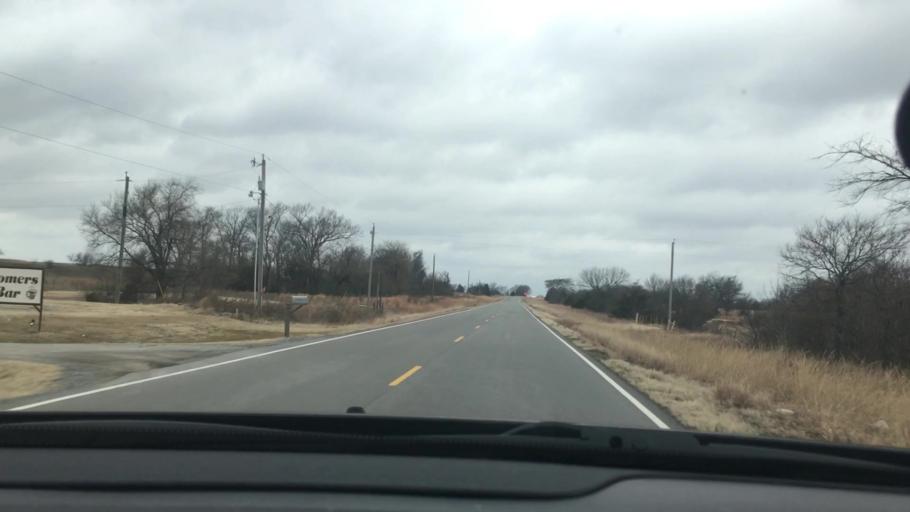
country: US
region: Oklahoma
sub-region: Atoka County
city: Atoka
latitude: 34.3747
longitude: -96.1885
